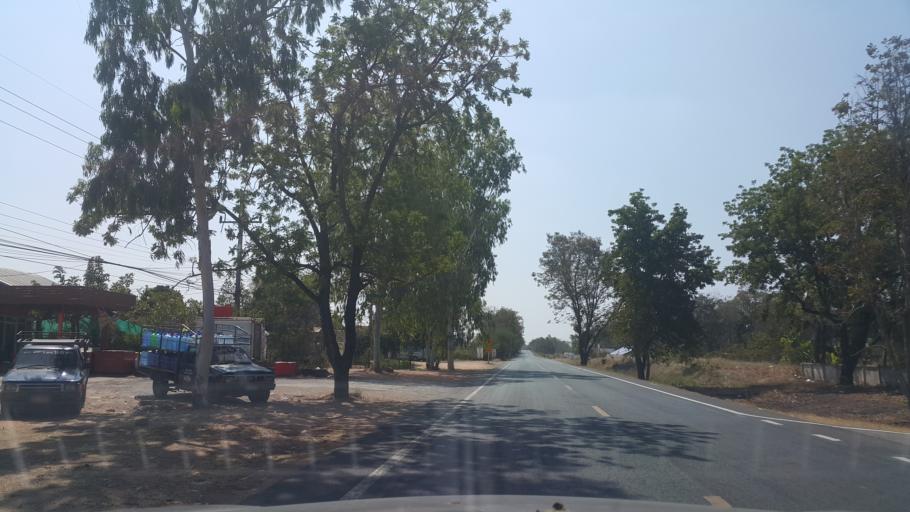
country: TH
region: Nakhon Ratchasima
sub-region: Amphoe Kaeng Sanam Nang
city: Kaeng Sanam Nang
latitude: 15.6874
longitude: 102.3300
